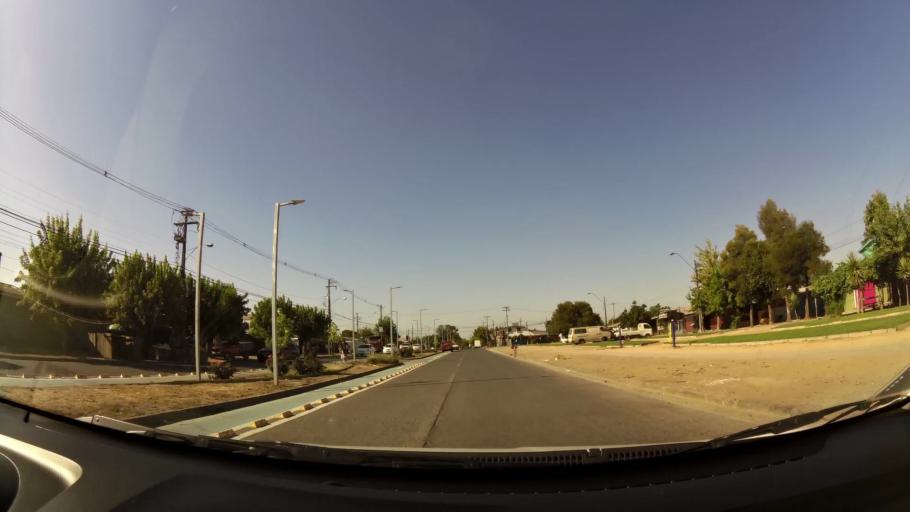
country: CL
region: Maule
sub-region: Provincia de Talca
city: Talca
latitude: -35.4465
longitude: -71.6550
